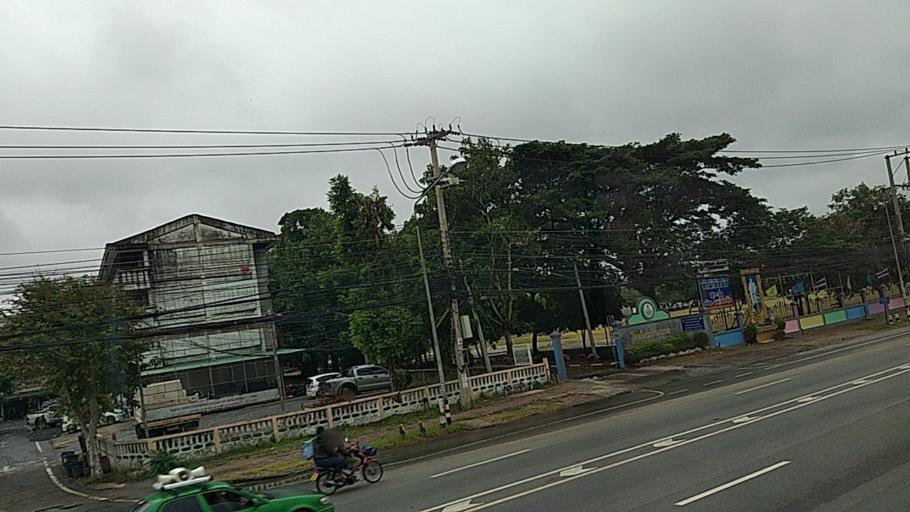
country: TH
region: Nakhon Ratchasima
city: Nakhon Ratchasima
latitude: 15.0308
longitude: 102.1408
